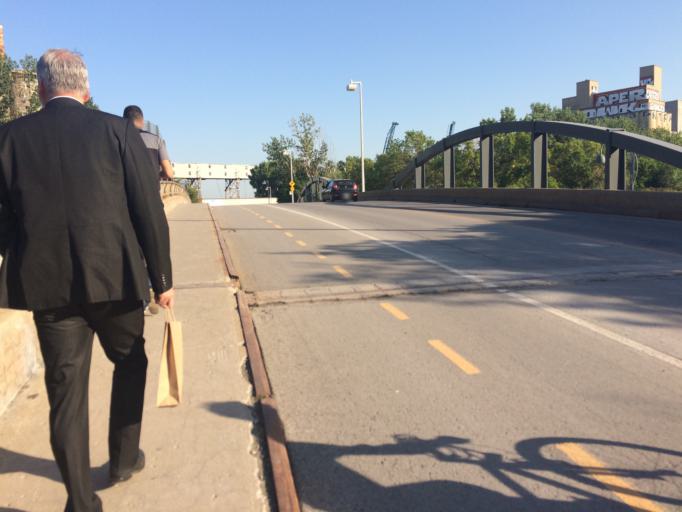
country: CA
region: Quebec
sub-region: Montreal
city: Montreal
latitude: 45.4961
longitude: -73.5523
